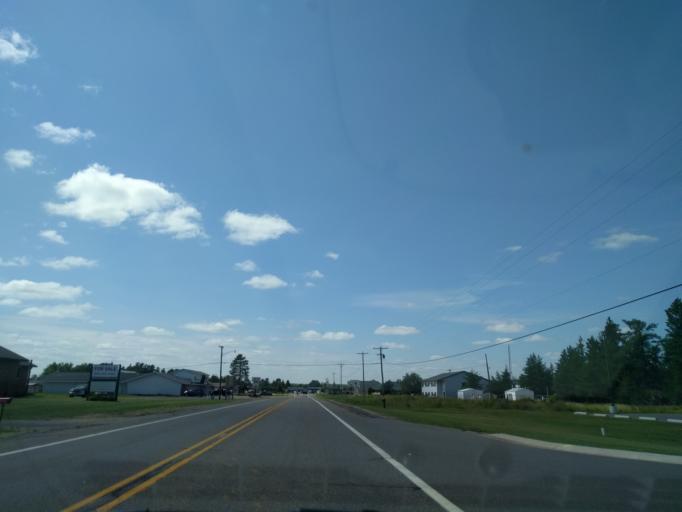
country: US
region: Michigan
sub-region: Marquette County
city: Gwinn
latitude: 46.2760
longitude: -87.4171
